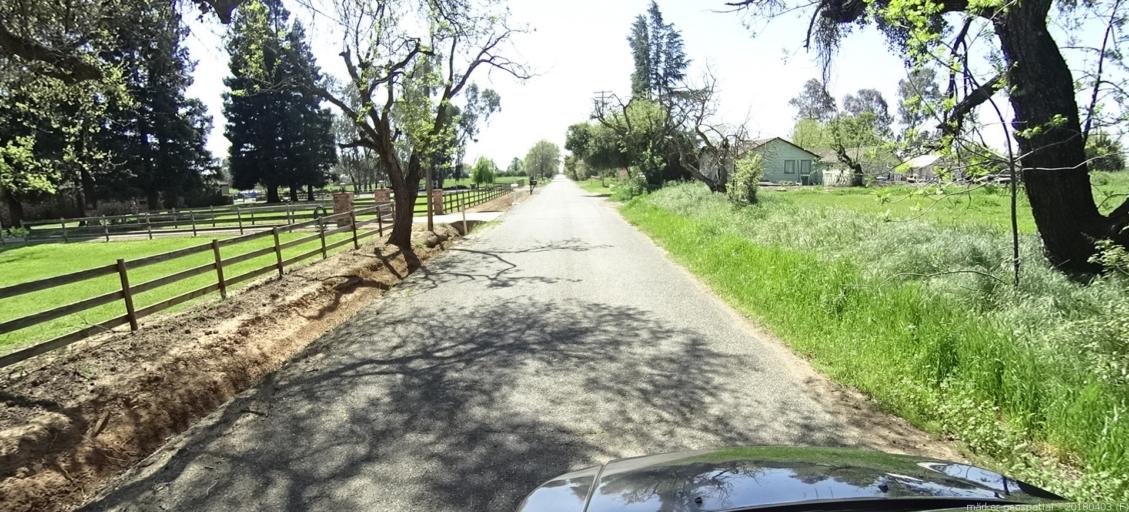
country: US
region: California
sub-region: Sacramento County
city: Wilton
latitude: 38.4017
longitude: -121.2873
